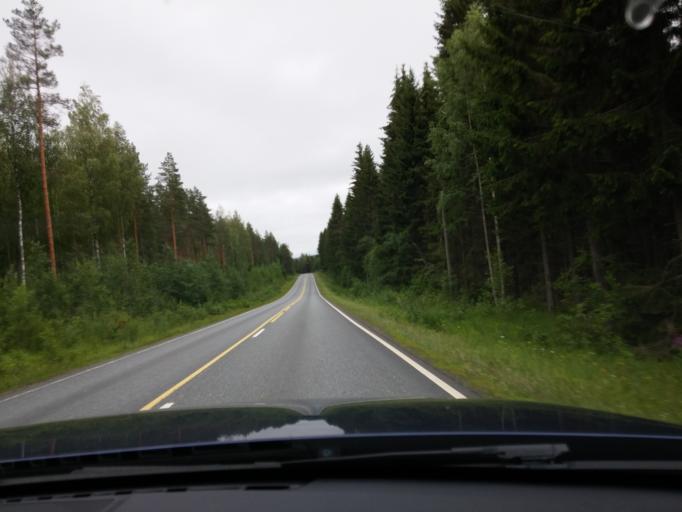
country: FI
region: Central Finland
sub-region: Joutsa
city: Joutsa
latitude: 61.8162
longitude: 25.9314
